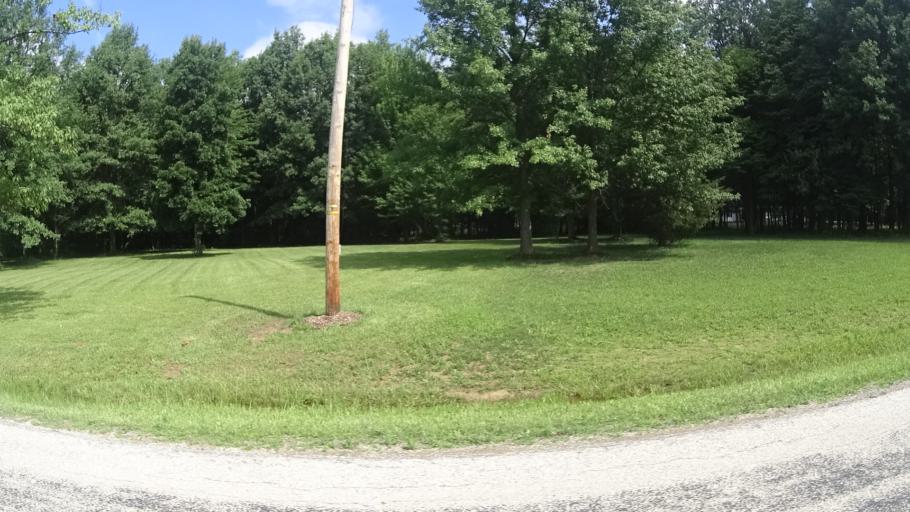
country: US
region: Ohio
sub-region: Huron County
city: Wakeman
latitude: 41.3143
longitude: -82.3941
